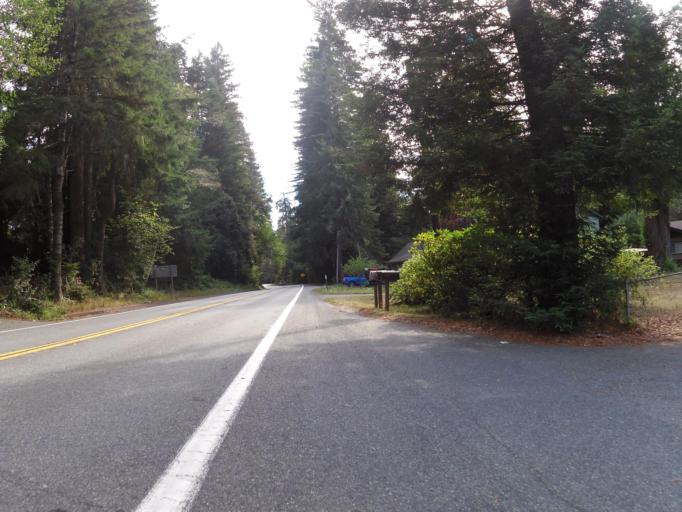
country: US
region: California
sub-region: Del Norte County
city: Bertsch-Oceanview
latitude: 41.8080
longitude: -124.0801
